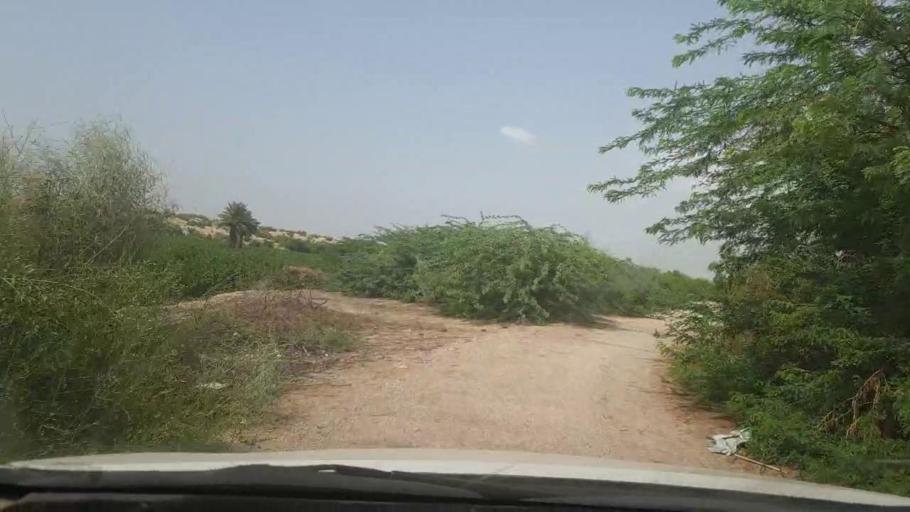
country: PK
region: Sindh
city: Kot Diji
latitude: 27.3361
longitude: 69.0400
